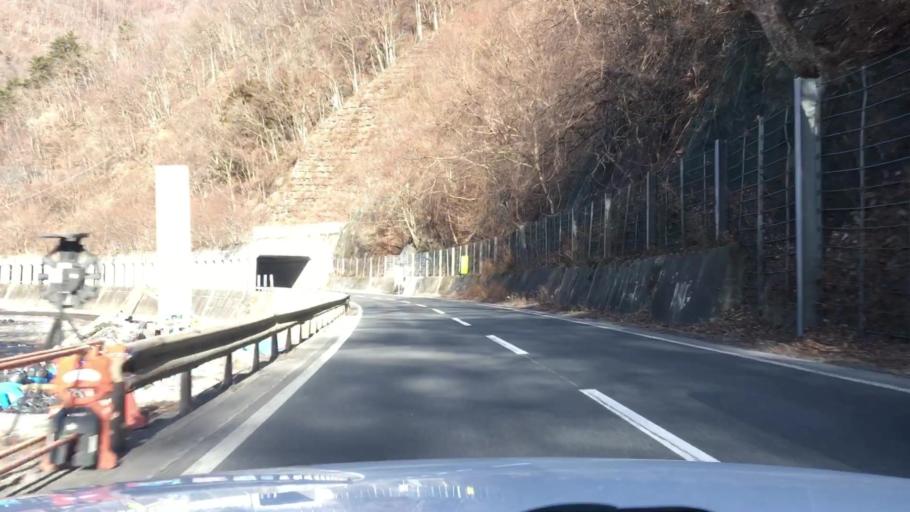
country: JP
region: Iwate
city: Miyako
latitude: 39.6039
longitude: 141.6530
